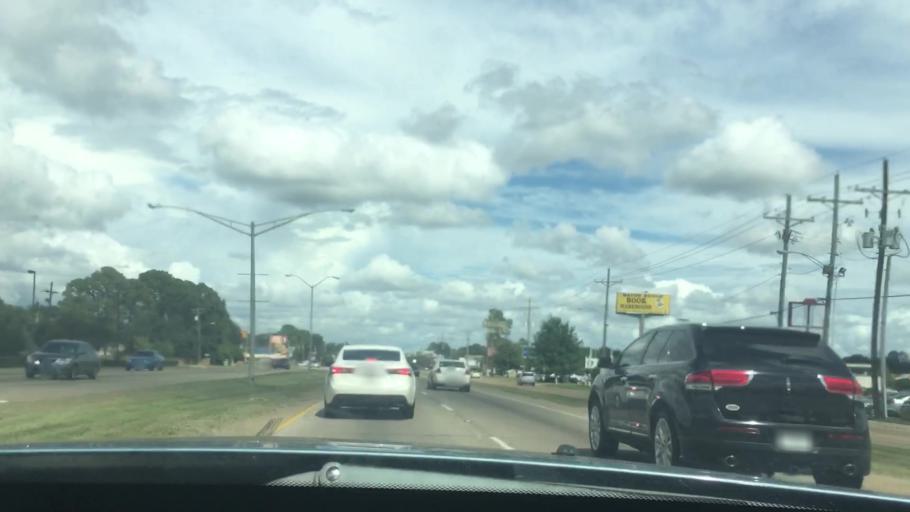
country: US
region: Louisiana
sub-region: East Baton Rouge Parish
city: Westminster
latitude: 30.4551
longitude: -91.0815
